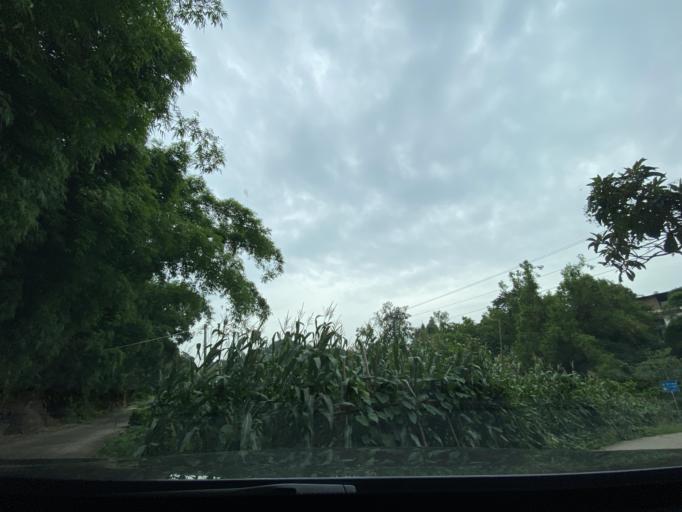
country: CN
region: Sichuan
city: Jiancheng
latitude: 30.3868
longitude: 104.4958
